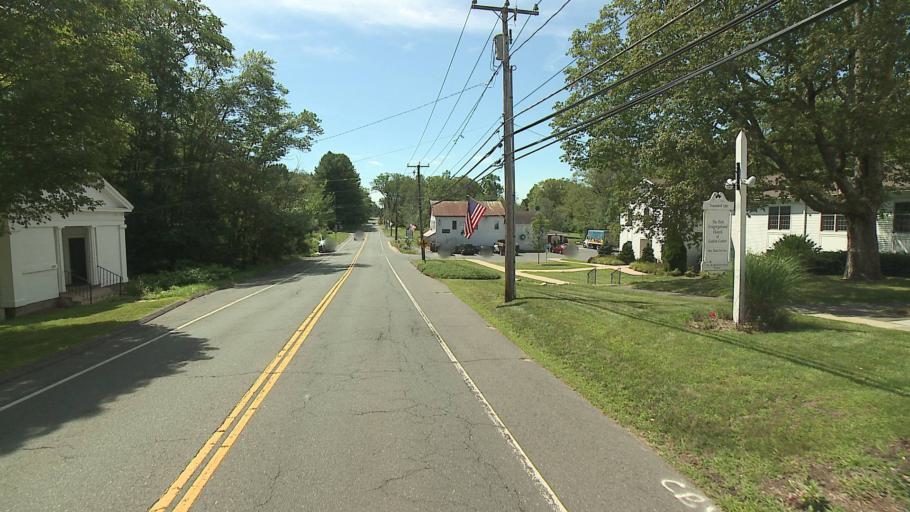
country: US
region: Connecticut
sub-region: Hartford County
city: Canton Valley
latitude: 41.8547
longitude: -72.9165
